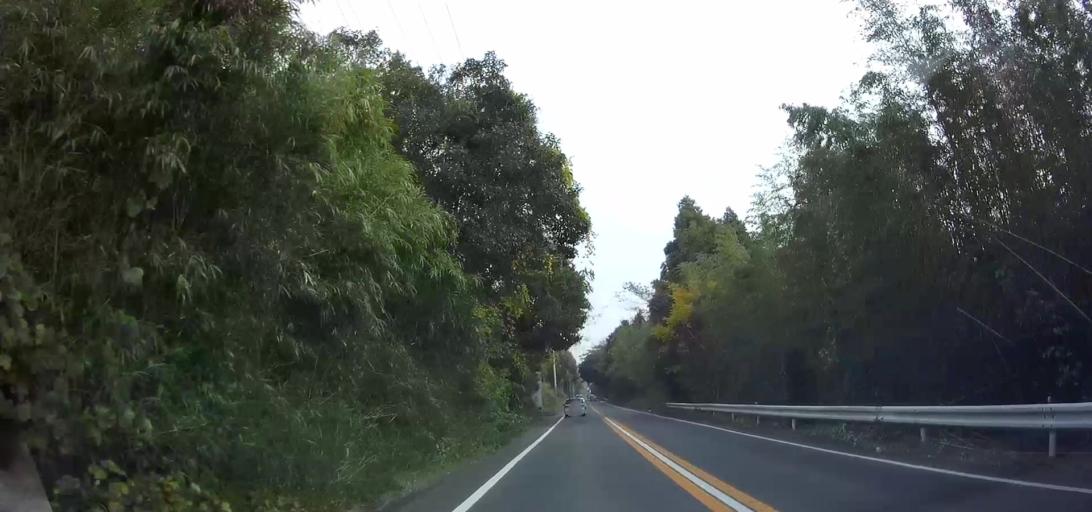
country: JP
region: Nagasaki
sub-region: Isahaya-shi
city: Isahaya
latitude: 32.7988
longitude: 130.1255
